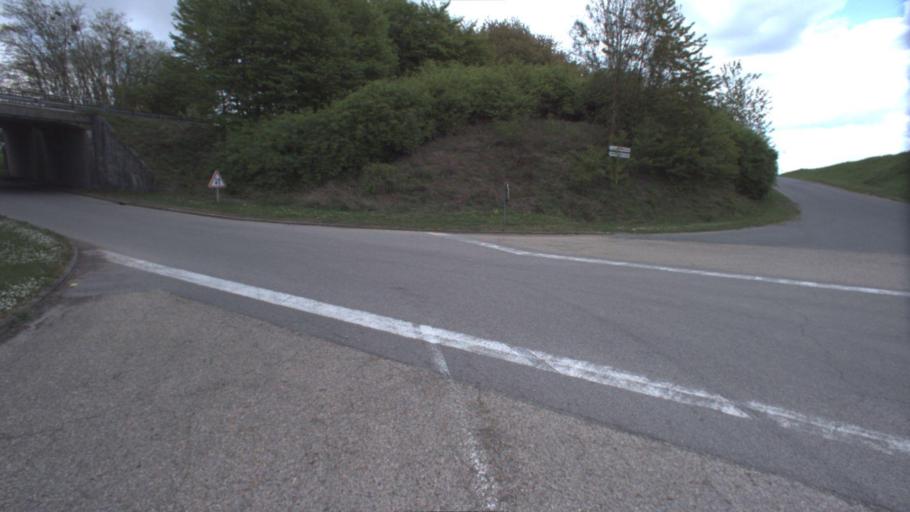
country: FR
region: Ile-de-France
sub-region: Departement de Seine-et-Marne
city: Jouy-le-Chatel
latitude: 48.6842
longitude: 3.0738
